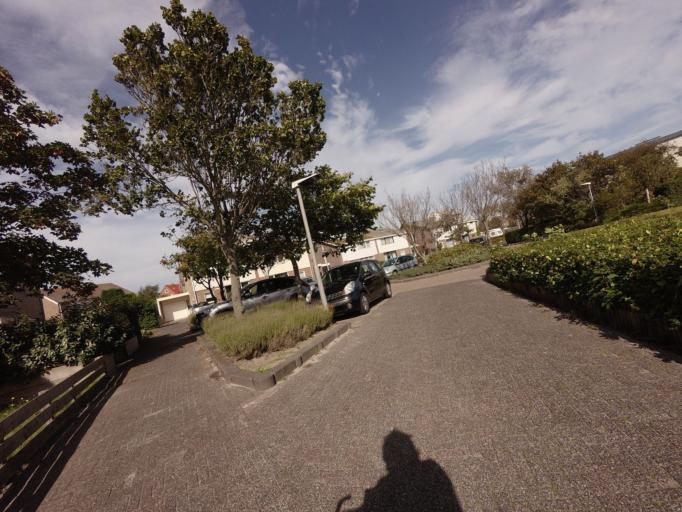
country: NL
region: North Holland
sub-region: Gemeente Texel
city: Den Burg
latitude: 53.1001
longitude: 4.7654
